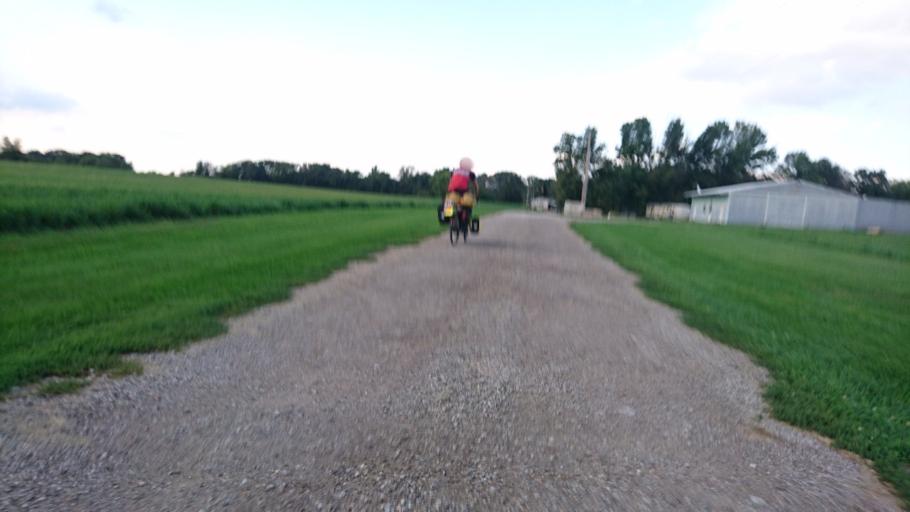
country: US
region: Illinois
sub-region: Logan County
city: Atlanta
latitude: 40.2244
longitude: -89.1975
